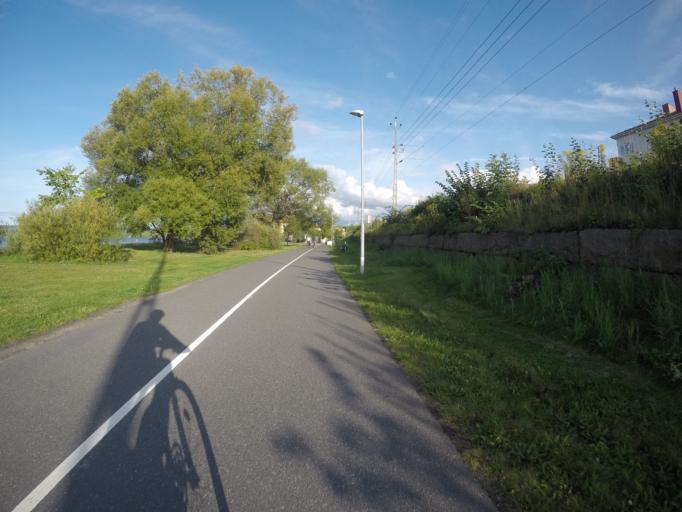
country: SE
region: Joenkoeping
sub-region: Jonkopings Kommun
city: Jonkoping
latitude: 57.7821
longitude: 14.1874
